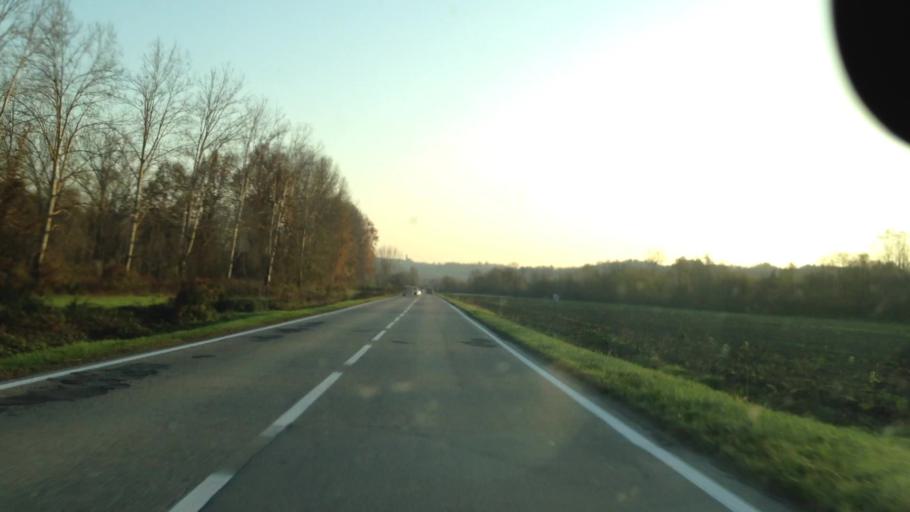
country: IT
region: Piedmont
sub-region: Provincia di Asti
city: Cunico
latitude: 45.0501
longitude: 8.1122
